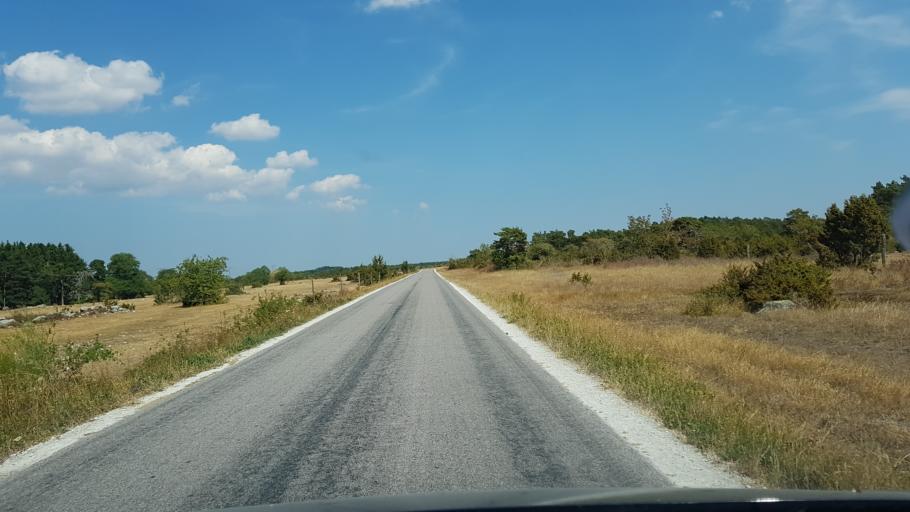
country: SE
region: Gotland
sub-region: Gotland
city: Visby
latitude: 57.6593
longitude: 18.3702
